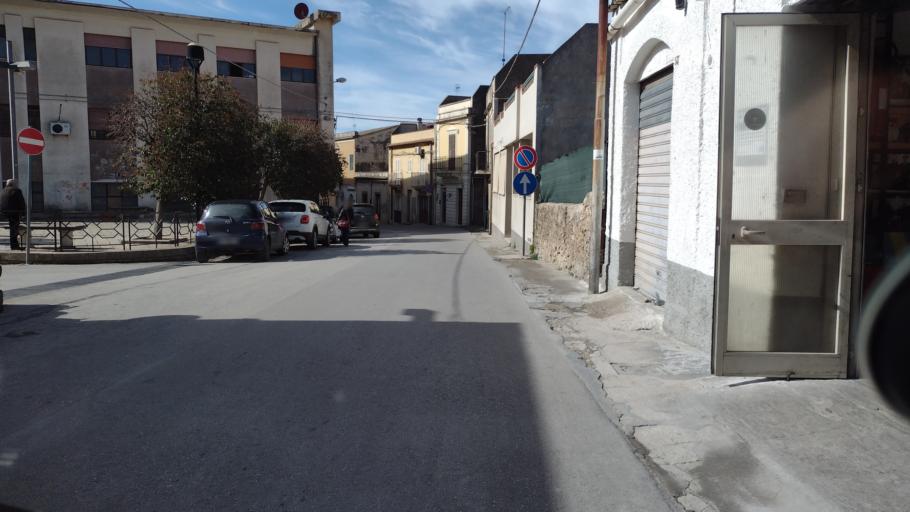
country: IT
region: Sicily
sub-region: Provincia di Siracusa
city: Noto
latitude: 36.8942
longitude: 15.0658
